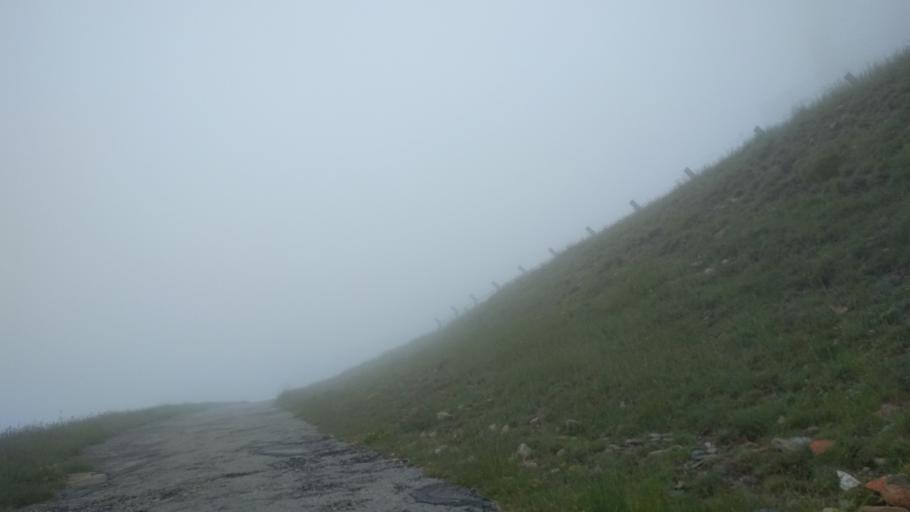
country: ES
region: Catalonia
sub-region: Provincia de Barcelona
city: Fogars de Montclus
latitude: 41.7745
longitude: 2.4373
